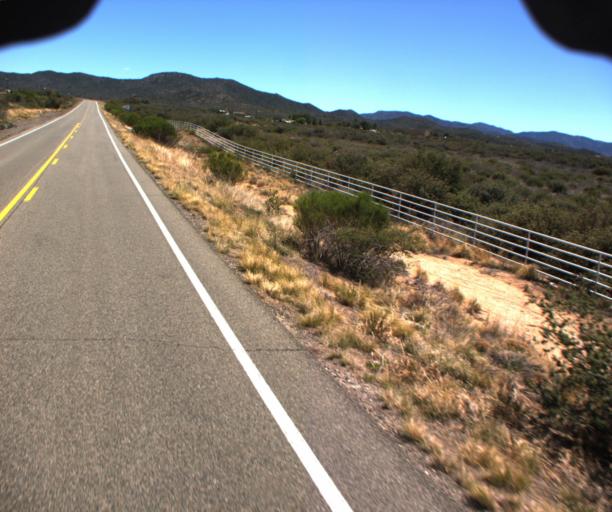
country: US
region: Arizona
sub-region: Yavapai County
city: Prescott
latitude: 34.4171
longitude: -112.5995
